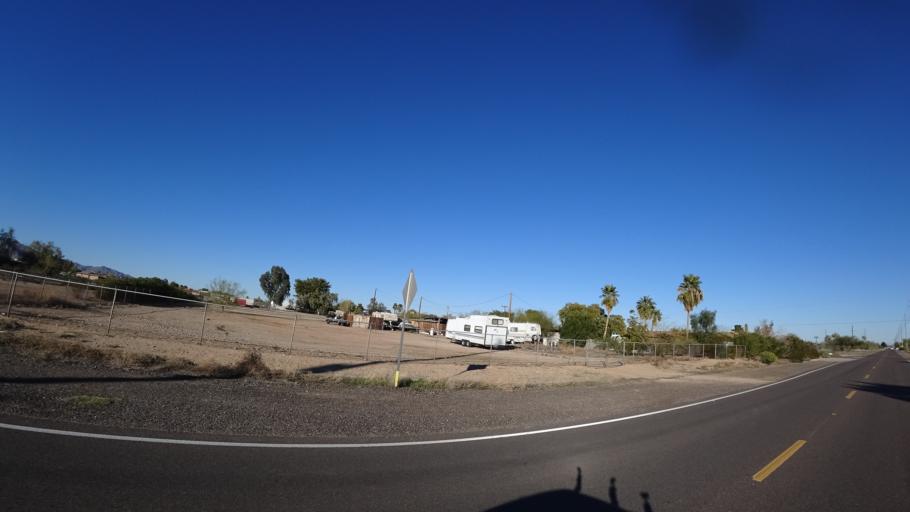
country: US
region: Arizona
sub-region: Maricopa County
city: Citrus Park
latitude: 33.4647
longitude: -112.4733
